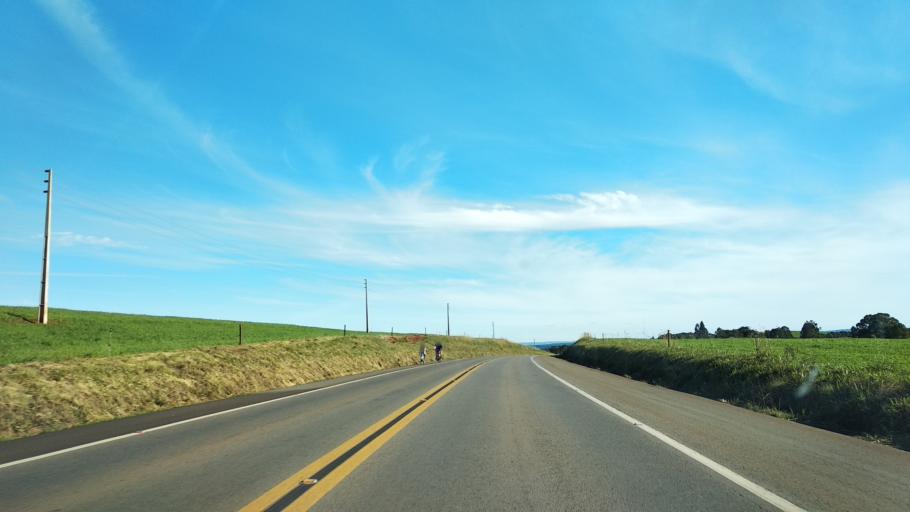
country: BR
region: Santa Catarina
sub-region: Celso Ramos
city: Celso Ramos
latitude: -27.5226
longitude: -51.3532
